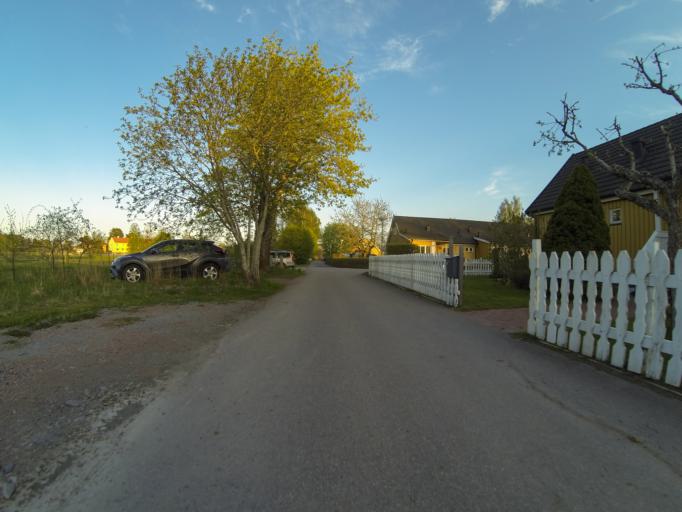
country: SE
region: Vaestmanland
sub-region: Vasteras
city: Vasteras
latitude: 59.5894
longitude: 16.6157
